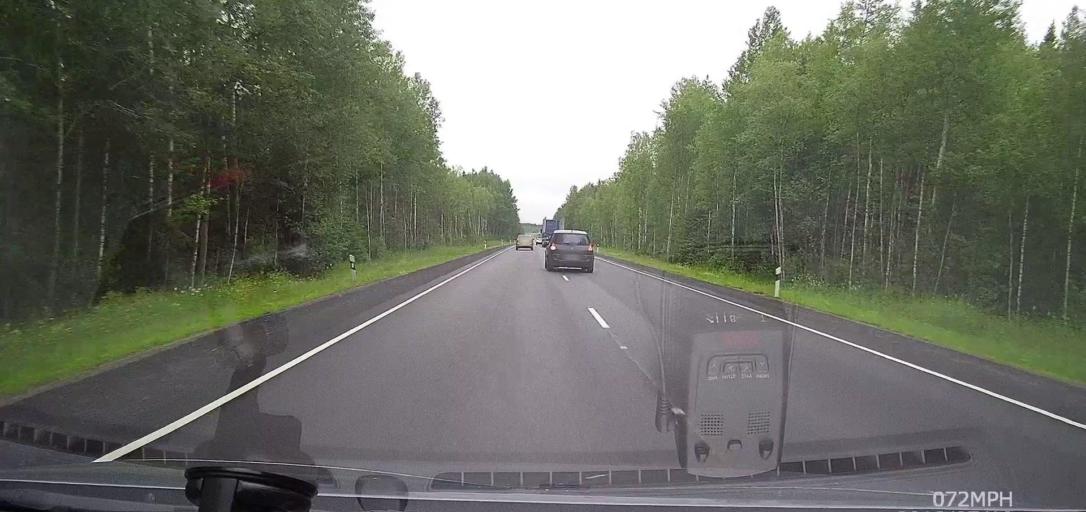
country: RU
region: Leningrad
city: Syas'stroy
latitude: 60.2618
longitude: 32.7759
